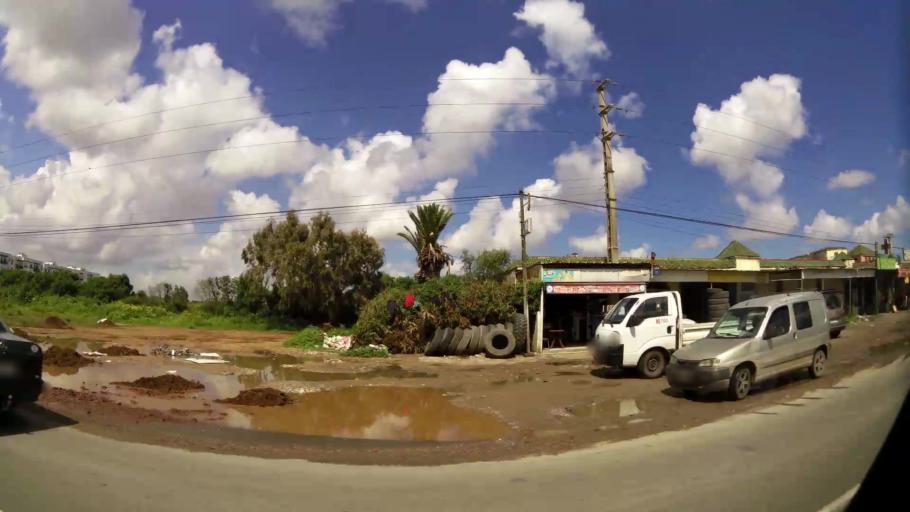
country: MA
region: Grand Casablanca
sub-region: Mediouna
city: Tit Mellil
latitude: 33.5533
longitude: -7.4878
